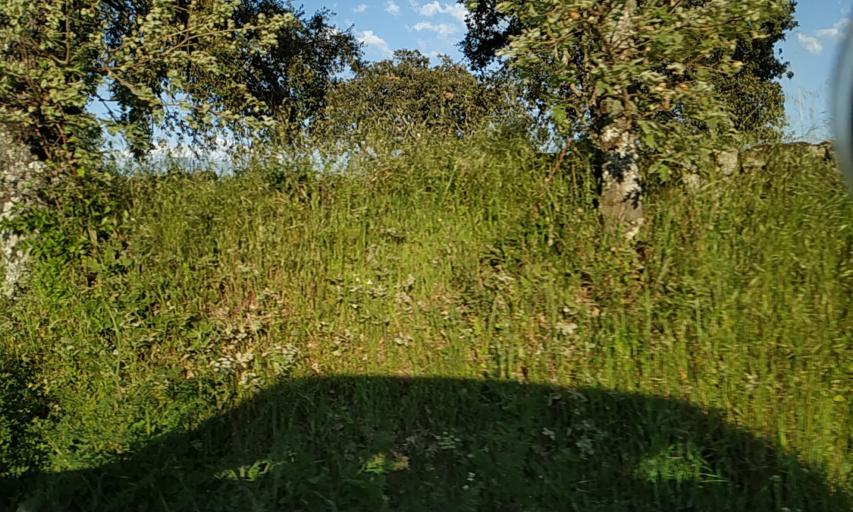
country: PT
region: Portalegre
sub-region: Portalegre
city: Reguengo
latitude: 39.3447
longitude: -7.4088
